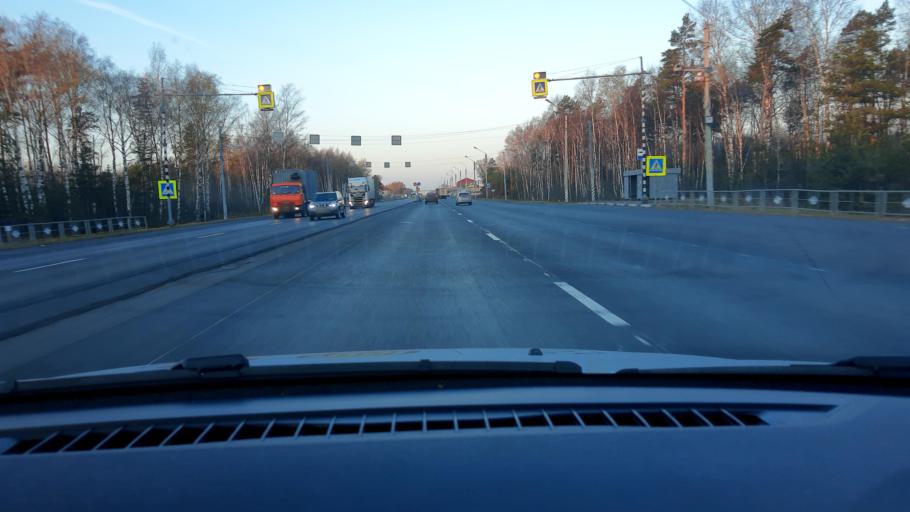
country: RU
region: Nizjnij Novgorod
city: Babino
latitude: 56.3049
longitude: 43.6327
